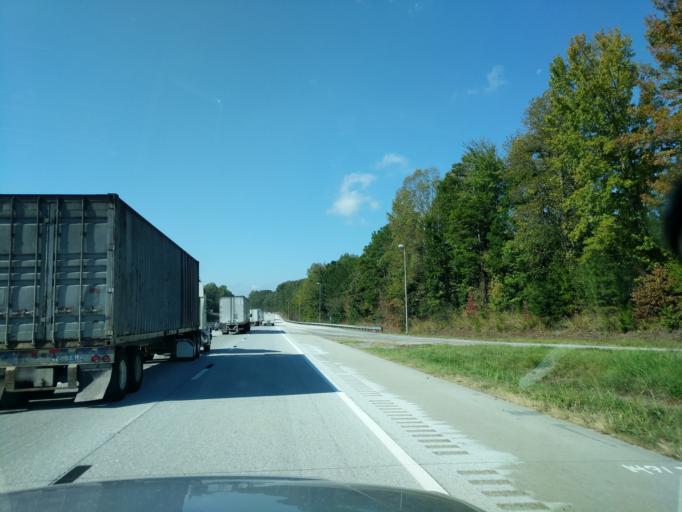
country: US
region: South Carolina
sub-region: Anderson County
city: Northlake
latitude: 34.6339
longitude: -82.5959
